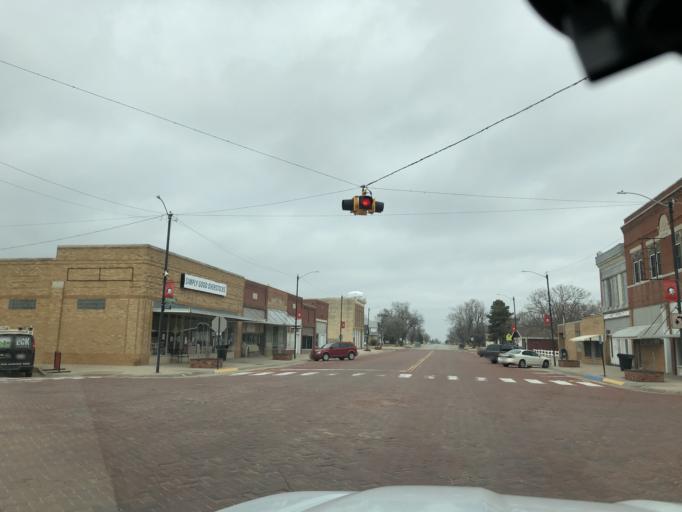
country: US
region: Kansas
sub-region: Stafford County
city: Stafford
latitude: 37.9617
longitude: -98.6004
